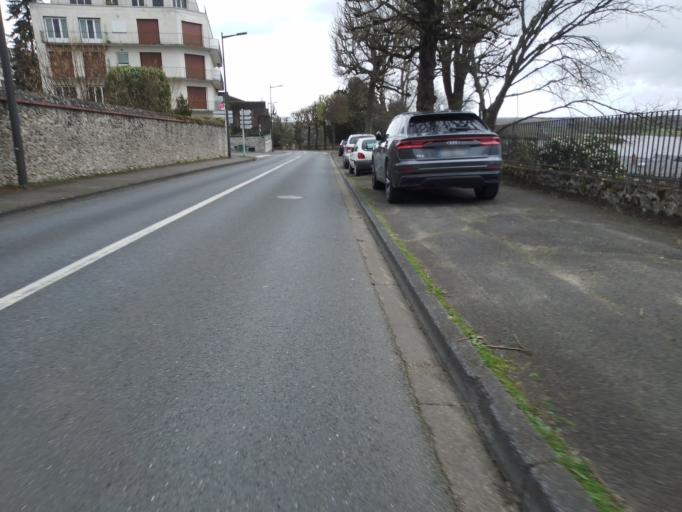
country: FR
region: Centre
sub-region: Departement du Loir-et-Cher
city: Blois
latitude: 47.5905
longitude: 1.3402
